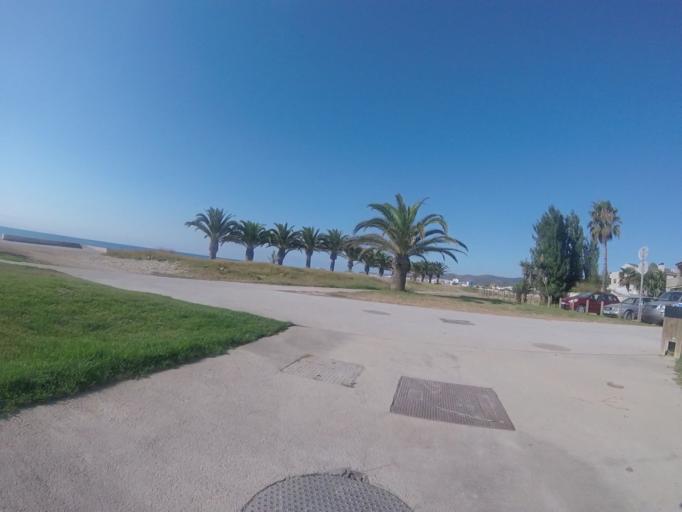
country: ES
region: Valencia
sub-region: Provincia de Castello
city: Benicarlo
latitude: 40.4100
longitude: 0.4289
